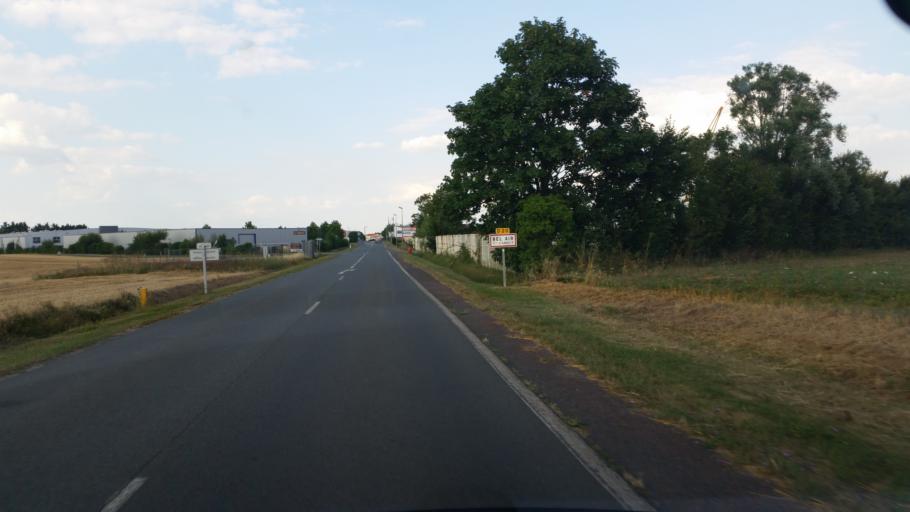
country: FR
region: Poitou-Charentes
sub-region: Departement de la Charente-Maritime
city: Andilly
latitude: 46.2587
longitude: -1.0158
